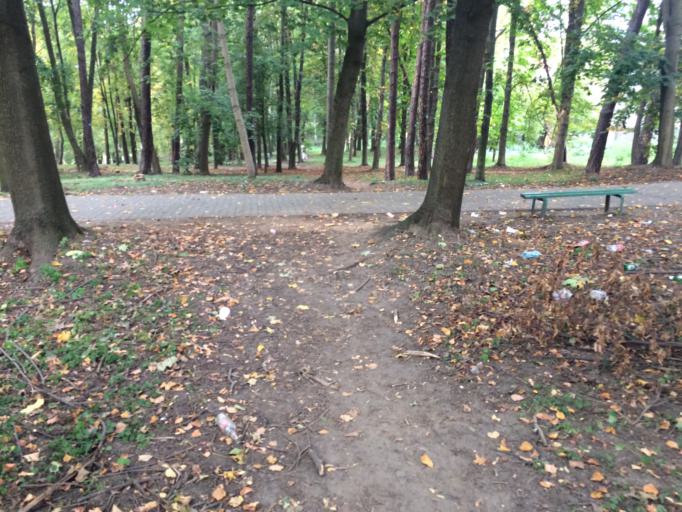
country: PL
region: Swietokrzyskie
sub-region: Powiat starachowicki
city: Starachowice
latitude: 51.0524
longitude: 21.0686
